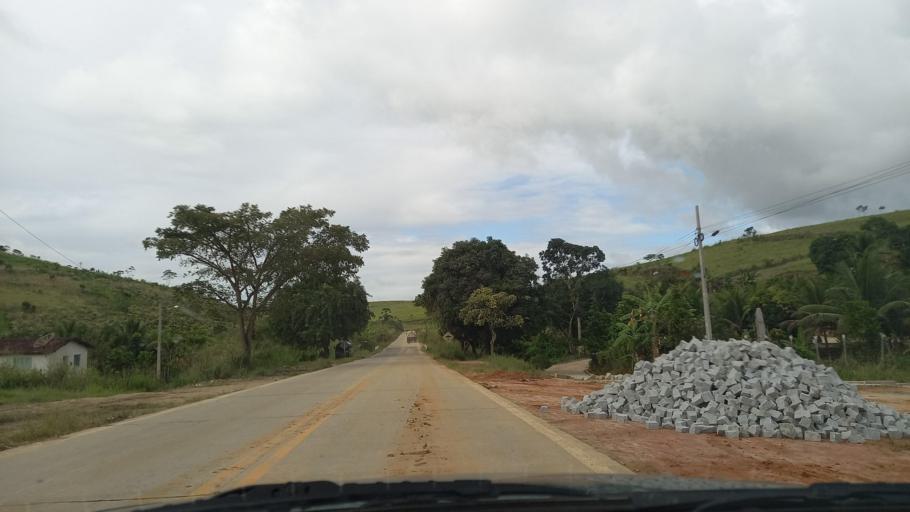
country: BR
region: Pernambuco
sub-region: Maraial
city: Maraial
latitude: -8.7602
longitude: -35.8545
